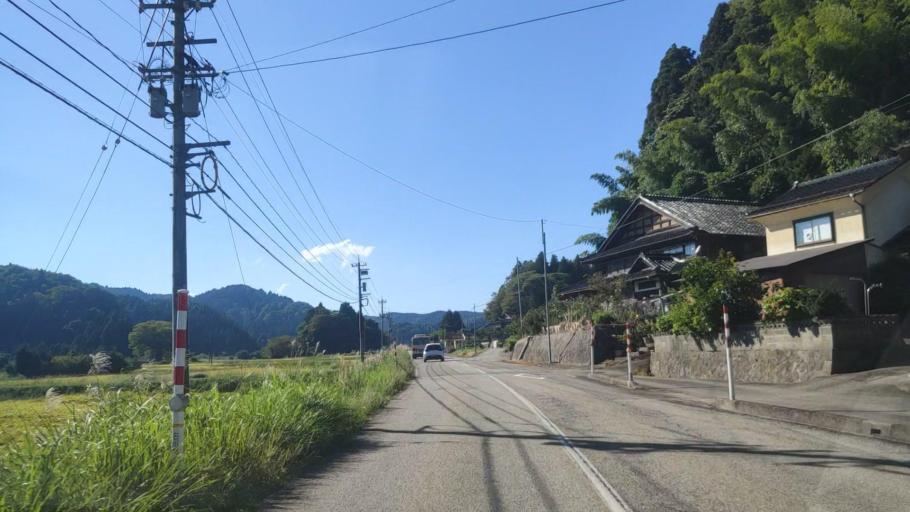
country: JP
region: Ishikawa
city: Nanao
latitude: 37.2783
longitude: 137.0513
